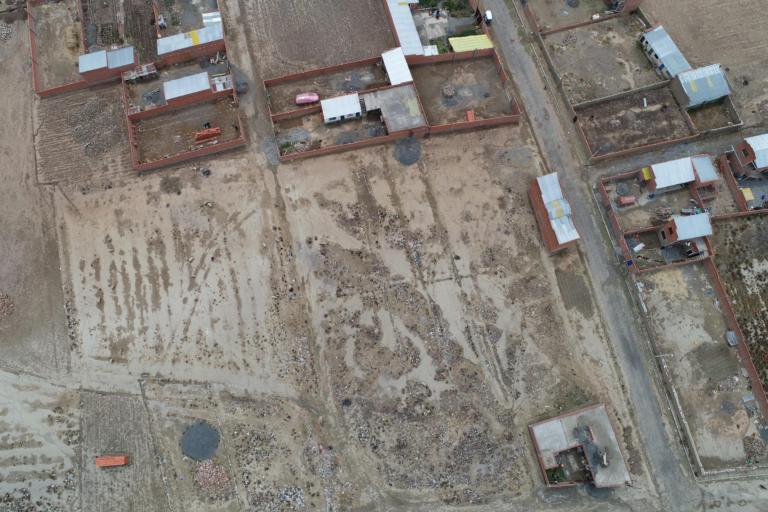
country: BO
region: La Paz
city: Achacachi
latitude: -16.0519
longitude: -68.6861
